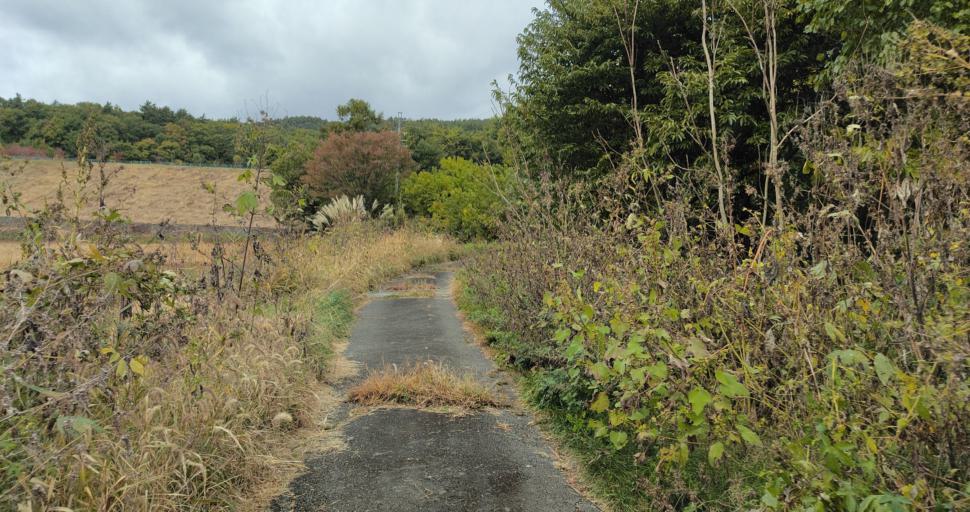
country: JP
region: Nagano
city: Komoro
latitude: 36.3624
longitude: 138.3840
